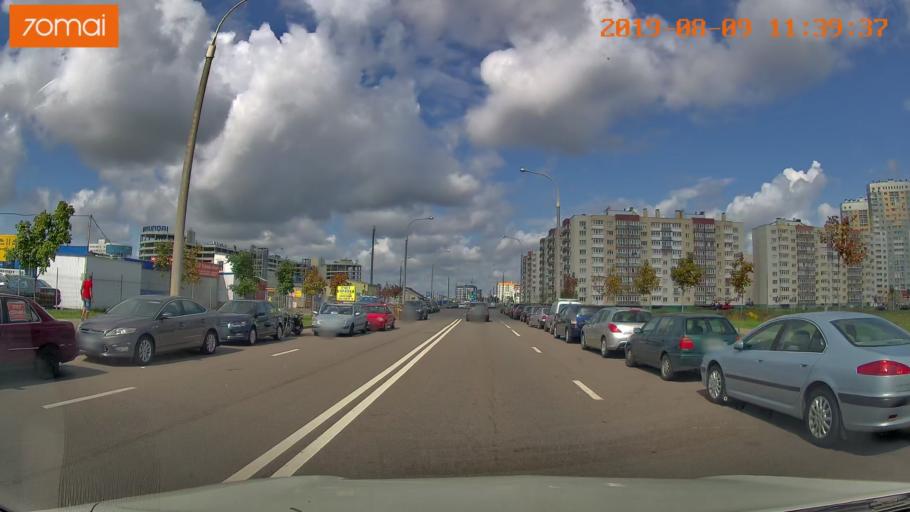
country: BY
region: Minsk
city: Zhdanovichy
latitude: 53.9337
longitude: 27.4630
